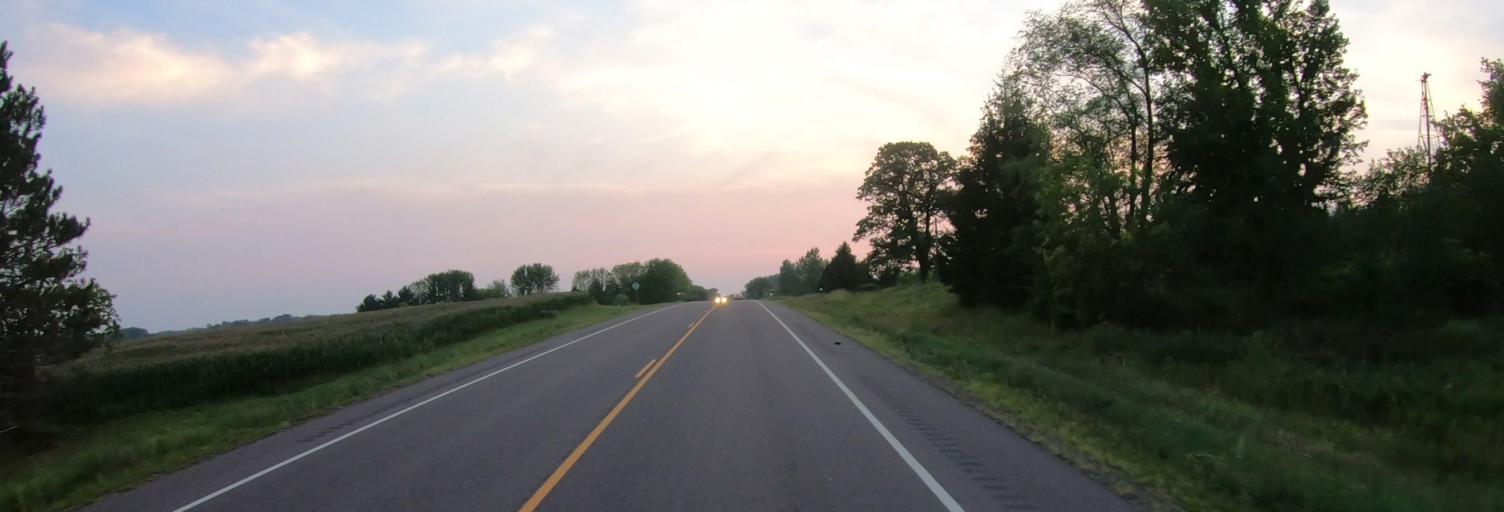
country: US
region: Minnesota
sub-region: Pine County
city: Rock Creek
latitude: 45.7735
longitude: -92.9422
